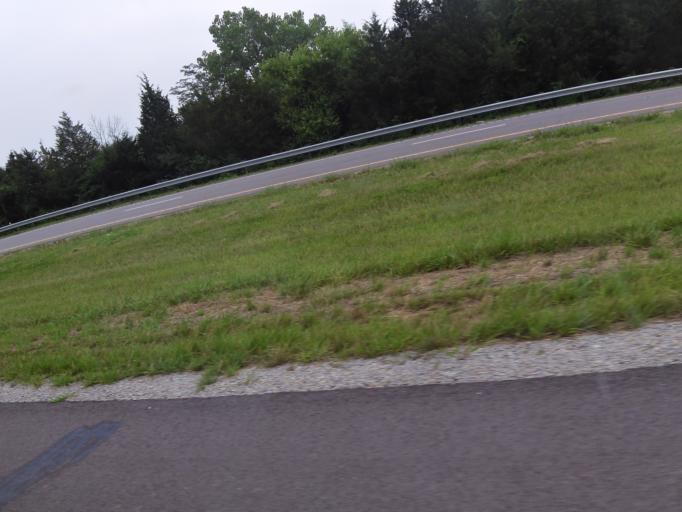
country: US
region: Ohio
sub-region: Warren County
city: Waynesville
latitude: 39.5343
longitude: -84.0792
